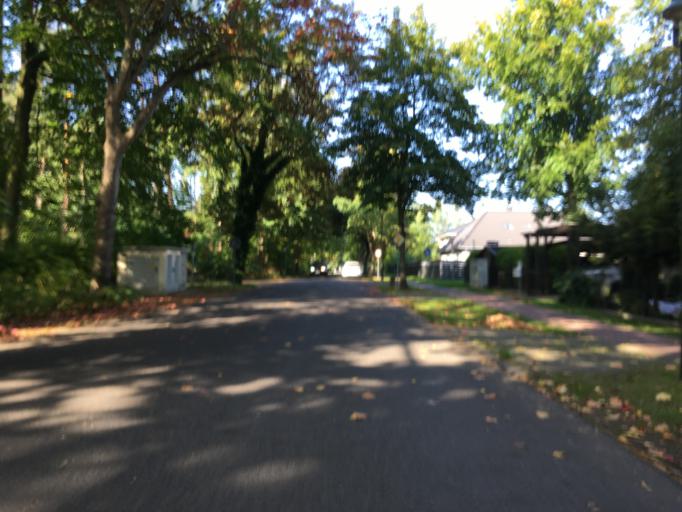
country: DE
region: Brandenburg
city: Wandlitz
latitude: 52.7438
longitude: 13.4726
